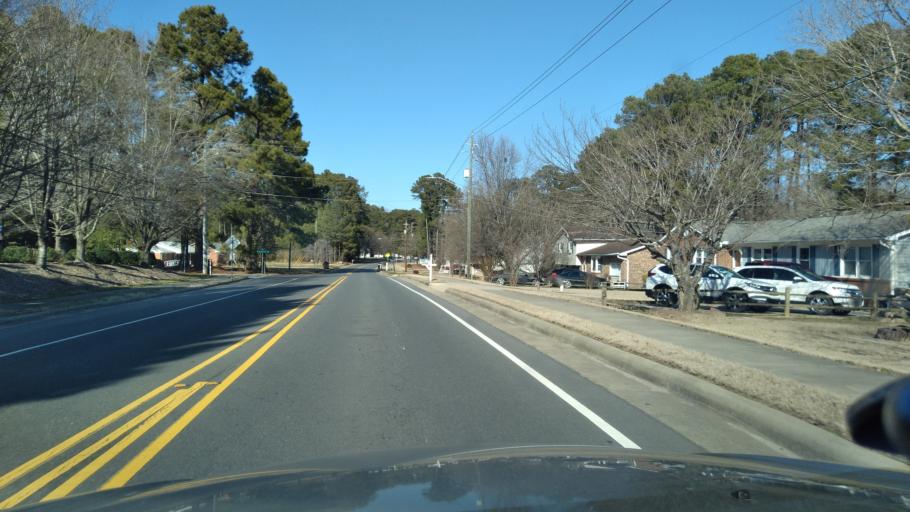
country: US
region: North Carolina
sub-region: Wake County
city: Garner
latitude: 35.6942
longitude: -78.6343
